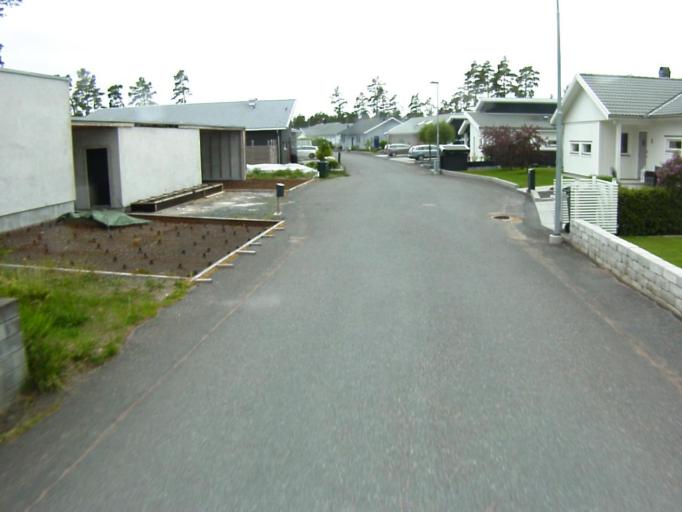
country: SE
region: Skane
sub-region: Kristianstads Kommun
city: Ahus
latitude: 55.9445
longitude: 14.2997
